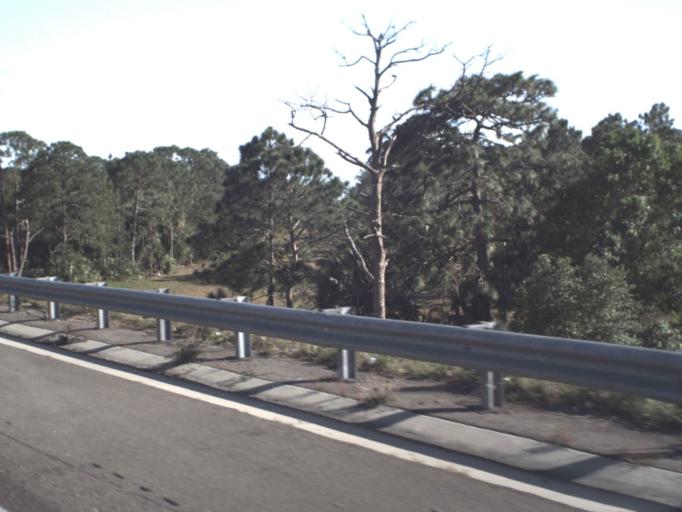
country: US
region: Florida
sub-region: Indian River County
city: Roseland
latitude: 27.8253
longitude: -80.5577
